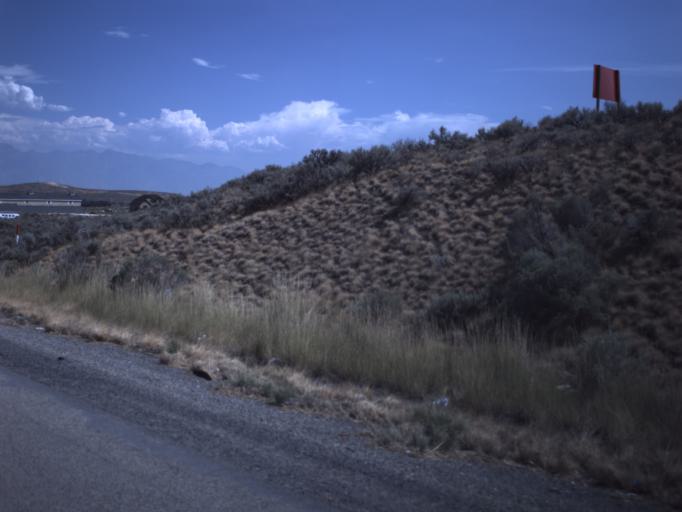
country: US
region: Utah
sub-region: Utah County
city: Eagle Mountain
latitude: 40.3802
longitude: -111.9863
